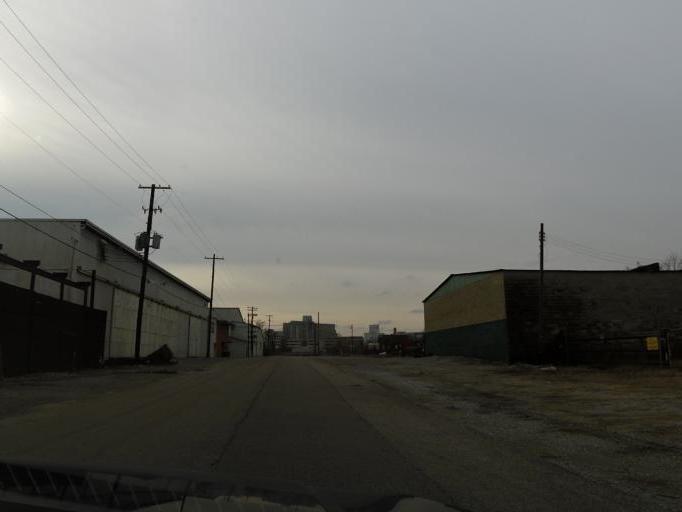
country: US
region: Alabama
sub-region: Montgomery County
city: Montgomery
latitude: 32.3865
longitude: -86.3121
